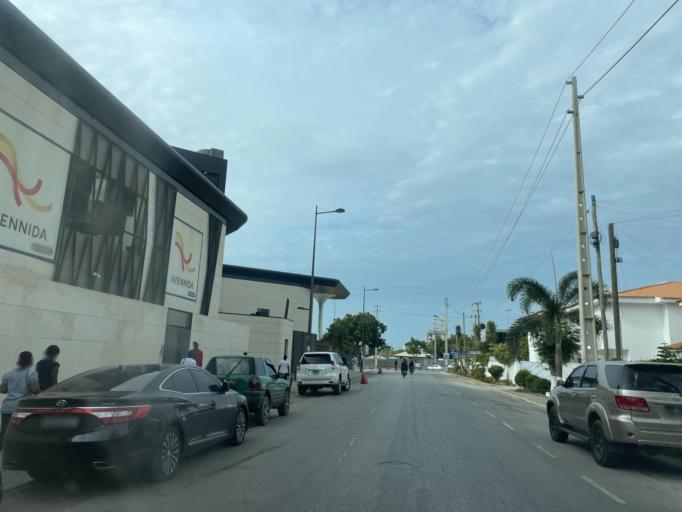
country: AO
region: Luanda
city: Luanda
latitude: -8.9201
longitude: 13.1809
